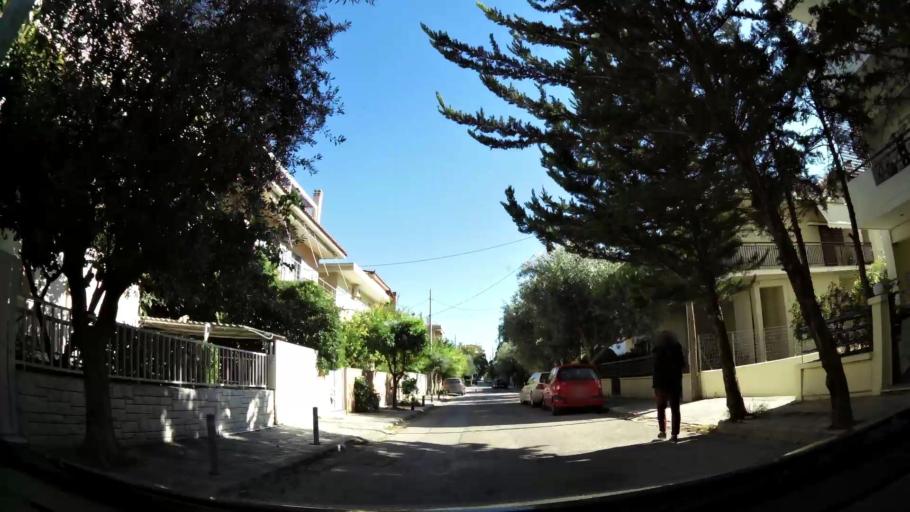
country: GR
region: Attica
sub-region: Nomarchia Athinas
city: Vrilissia
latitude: 38.0270
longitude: 23.8234
